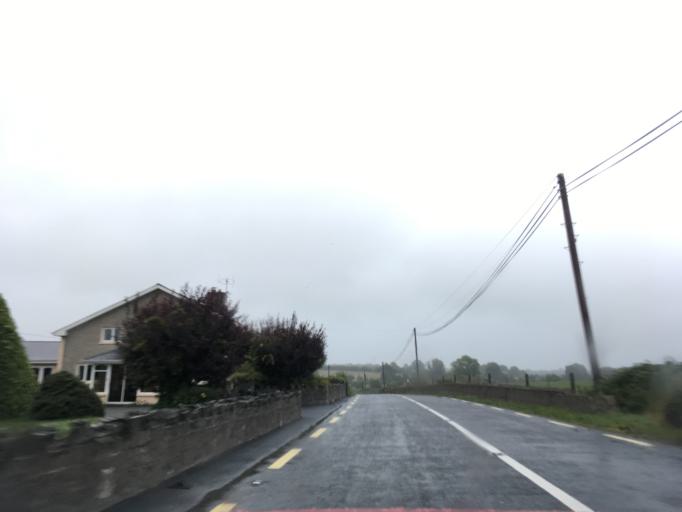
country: IE
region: Munster
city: Tipperary
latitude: 52.4839
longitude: -8.0726
